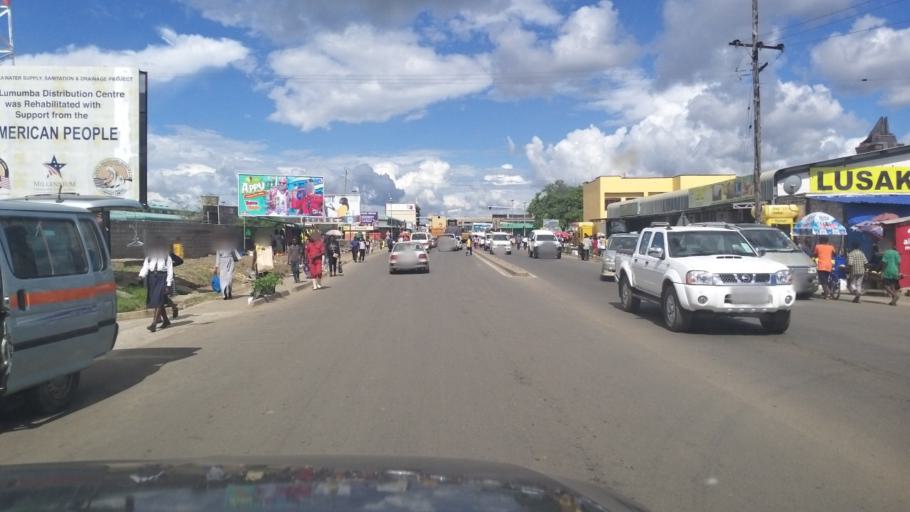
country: ZM
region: Lusaka
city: Lusaka
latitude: -15.4157
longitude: 28.2760
